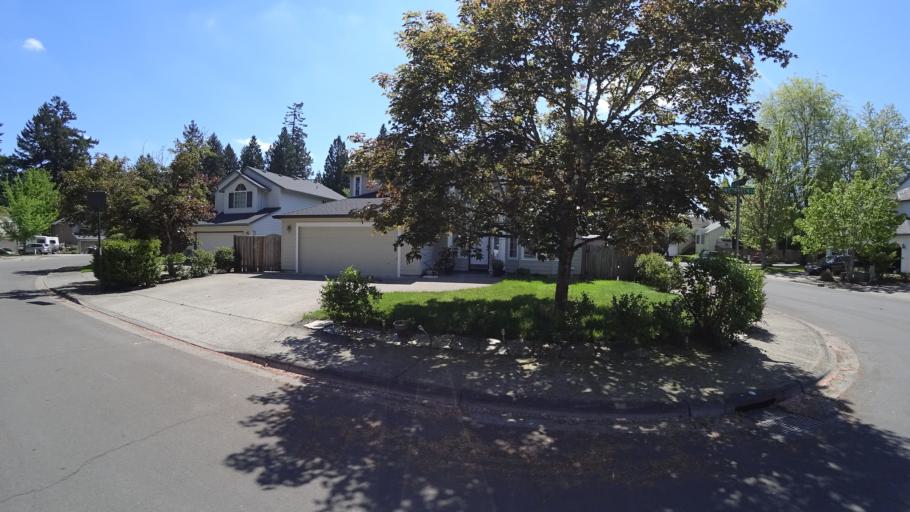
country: US
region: Oregon
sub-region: Washington County
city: Rockcreek
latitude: 45.5193
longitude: -122.8955
